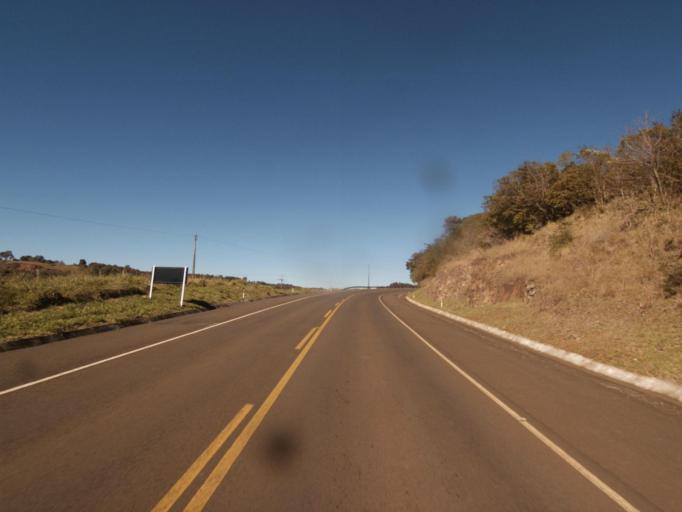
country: AR
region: Misiones
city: Bernardo de Irigoyen
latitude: -26.6926
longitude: -53.5410
